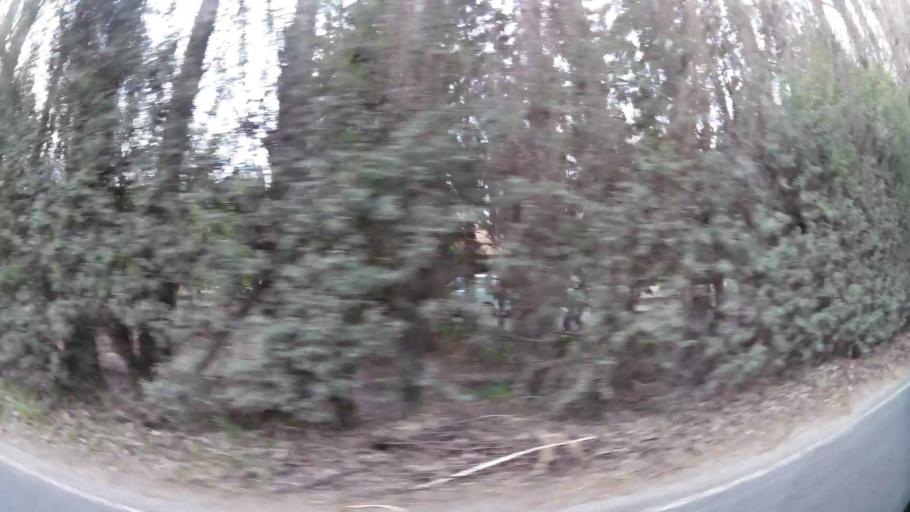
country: CL
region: Santiago Metropolitan
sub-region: Provincia de Chacabuco
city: Chicureo Abajo
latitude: -33.2702
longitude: -70.7113
